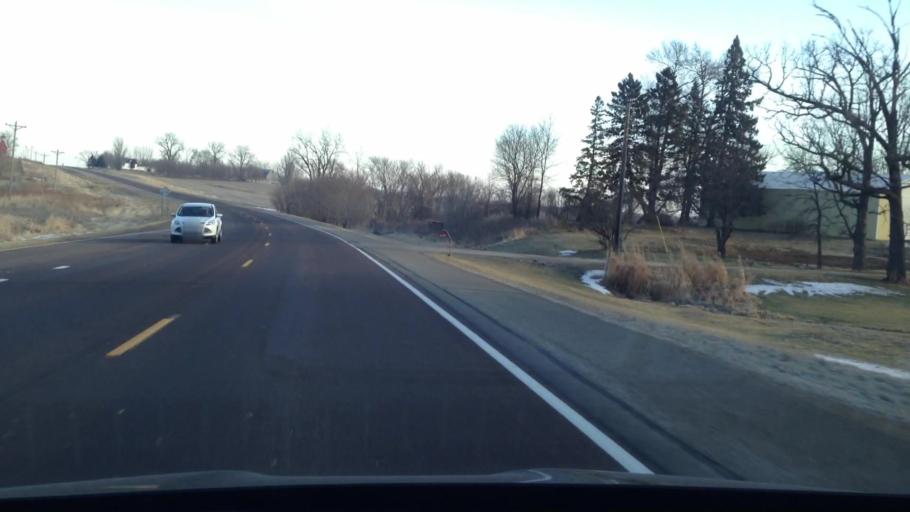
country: US
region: Minnesota
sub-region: Goodhue County
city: Goodhue
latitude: 44.3443
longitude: -92.6255
